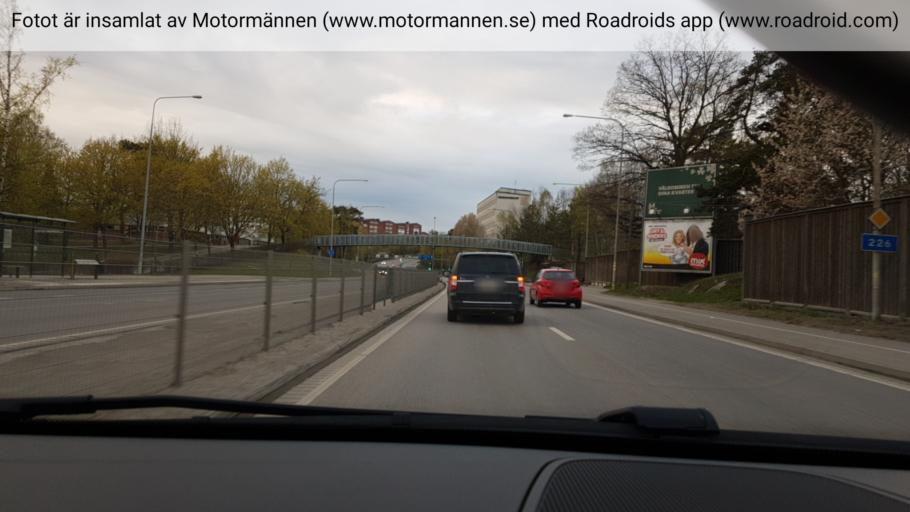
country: SE
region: Stockholm
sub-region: Huddinge Kommun
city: Huddinge
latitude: 59.2451
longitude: 17.9983
